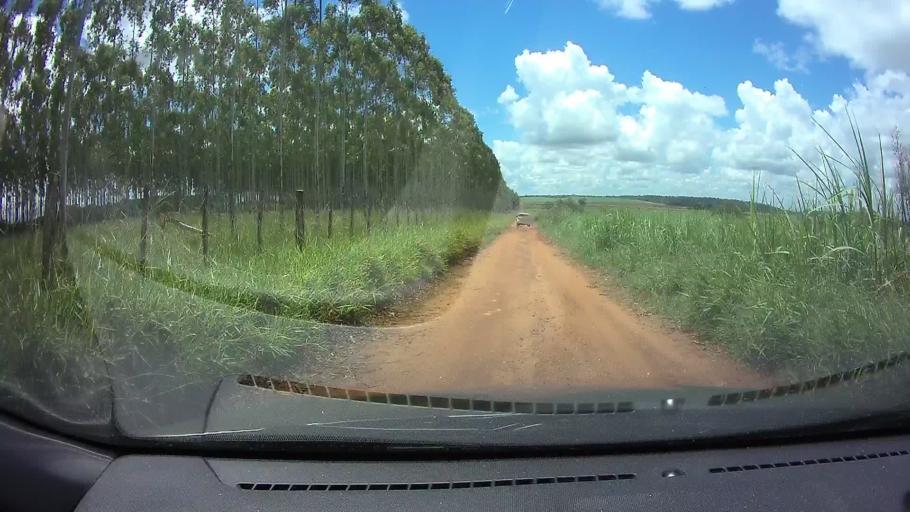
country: PY
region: Paraguari
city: La Colmena
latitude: -25.9669
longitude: -56.7339
